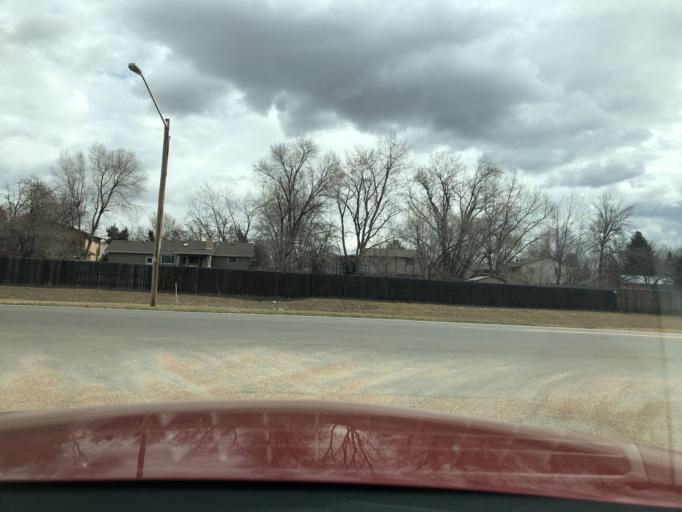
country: US
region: Colorado
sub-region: Boulder County
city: Gunbarrel
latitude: 40.0590
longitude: -105.1786
